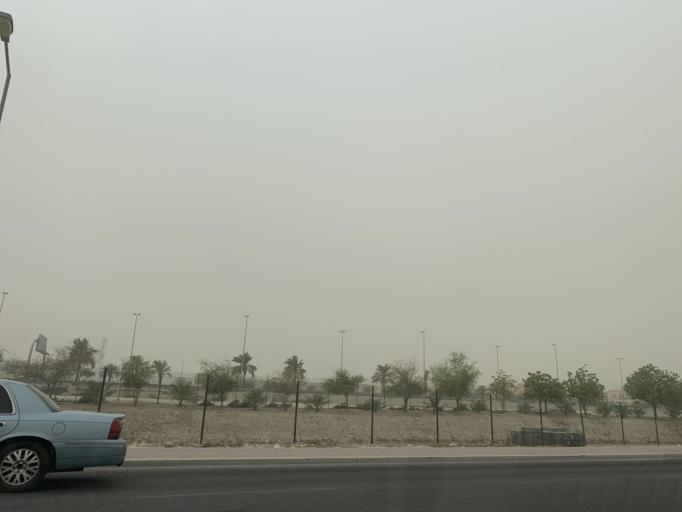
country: BH
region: Central Governorate
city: Madinat Hamad
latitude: 26.1299
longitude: 50.5088
